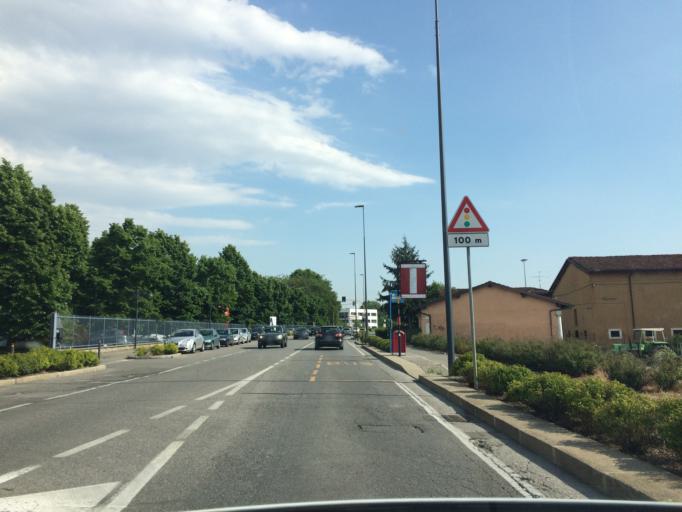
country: IT
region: Lombardy
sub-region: Provincia di Brescia
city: Buffalora-Bettole
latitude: 45.5166
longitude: 10.2495
